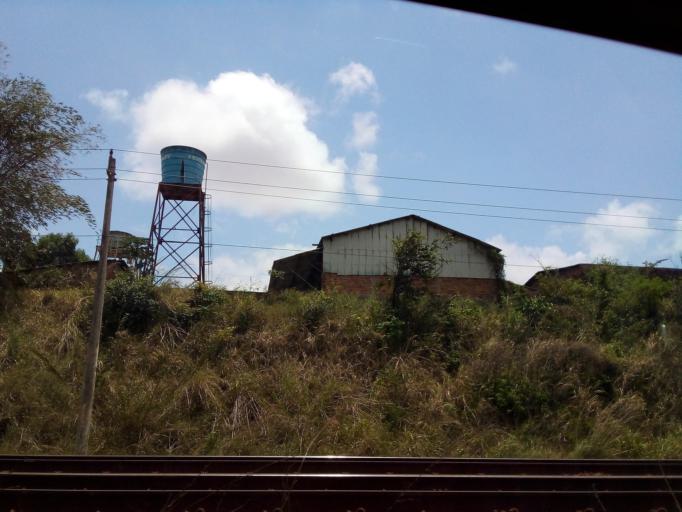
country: BR
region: Maranhao
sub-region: Sao Luis
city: Sao Luis
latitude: -2.7073
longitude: -44.3159
